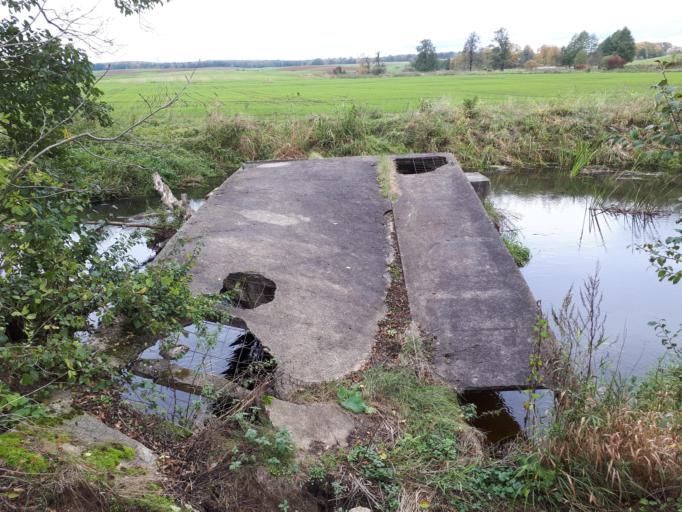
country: LT
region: Marijampoles apskritis
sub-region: Marijampole Municipality
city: Marijampole
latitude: 54.4311
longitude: 23.3844
